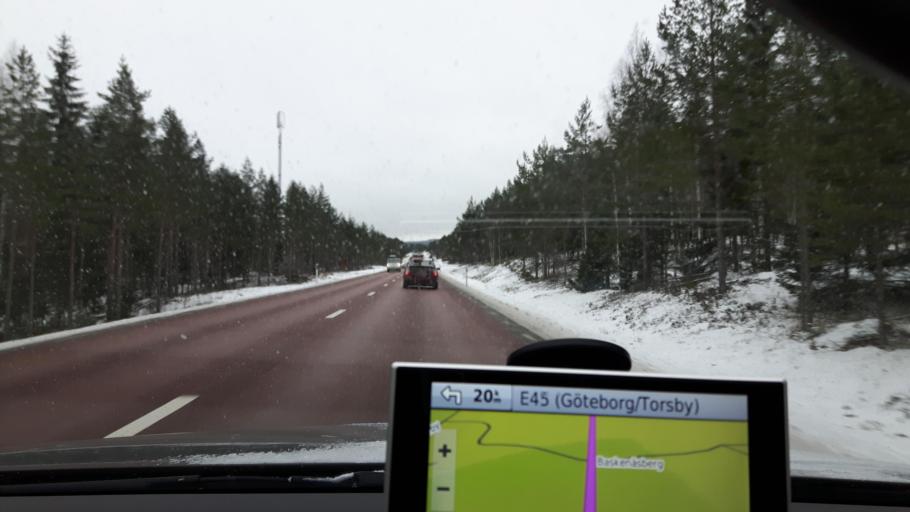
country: SE
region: Vaermland
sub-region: Hagfors Kommun
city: Ekshaerad
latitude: 60.4065
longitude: 13.2583
